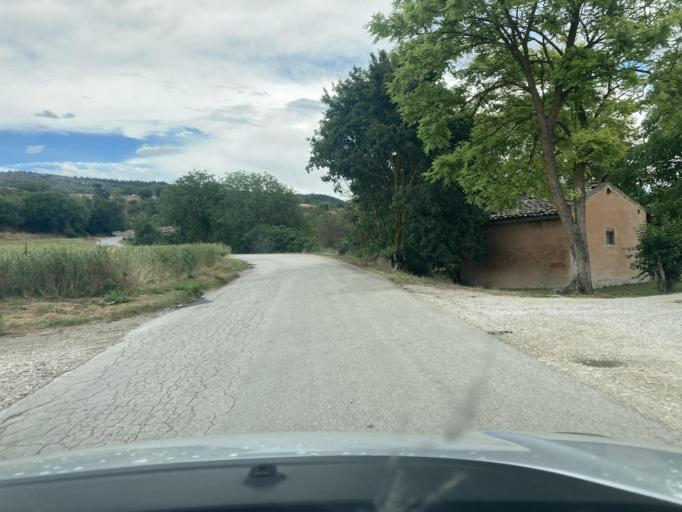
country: IT
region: Abruzzo
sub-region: Provincia dell' Aquila
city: San Demetrio Ne' Vestini
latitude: 42.2934
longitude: 13.5481
